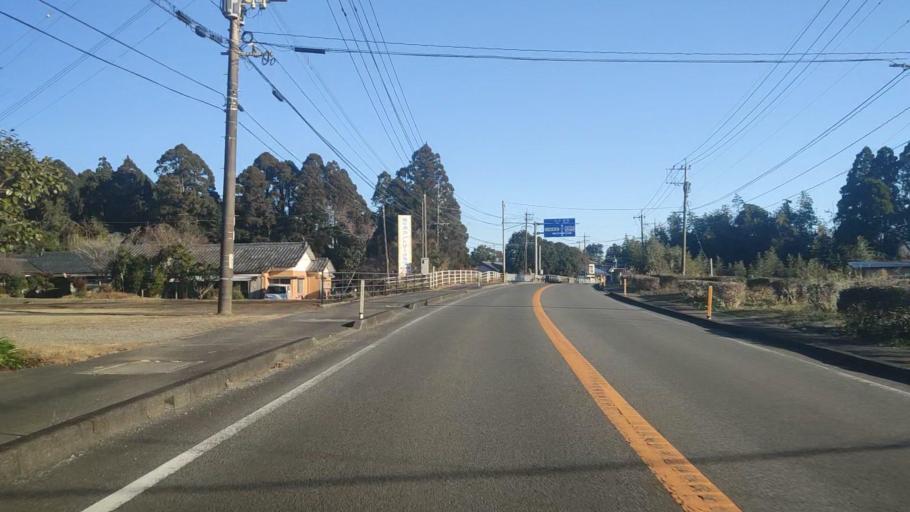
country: JP
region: Miyazaki
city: Takanabe
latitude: 32.3094
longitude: 131.5846
